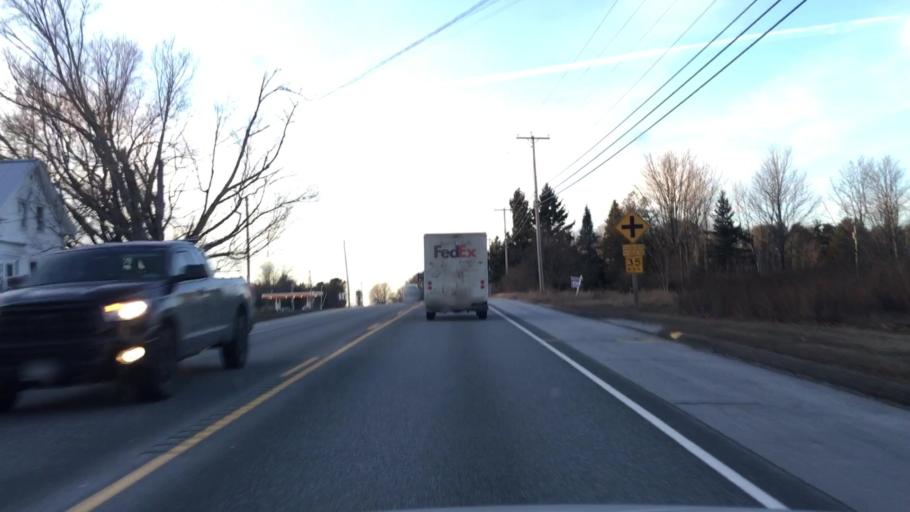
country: US
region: Maine
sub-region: Penobscot County
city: Holden
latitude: 44.7485
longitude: -68.6470
